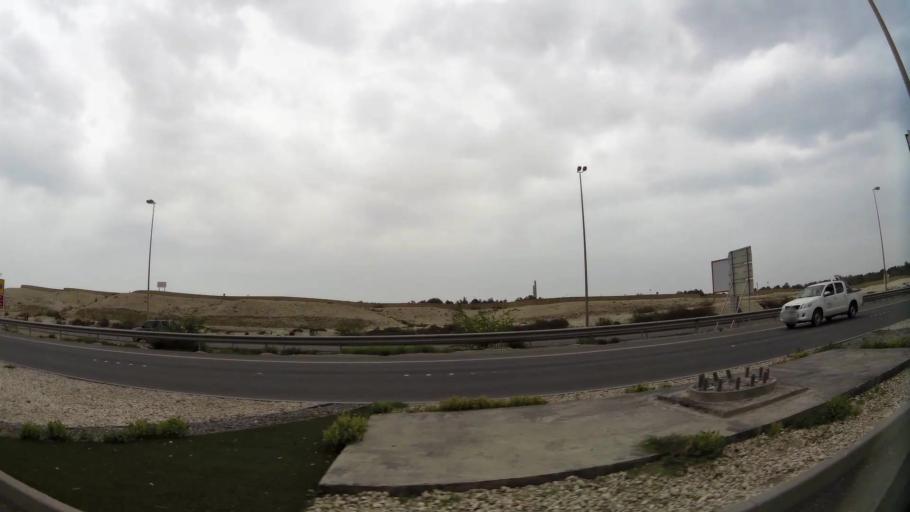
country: BH
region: Central Governorate
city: Dar Kulayb
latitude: 26.0587
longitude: 50.5127
